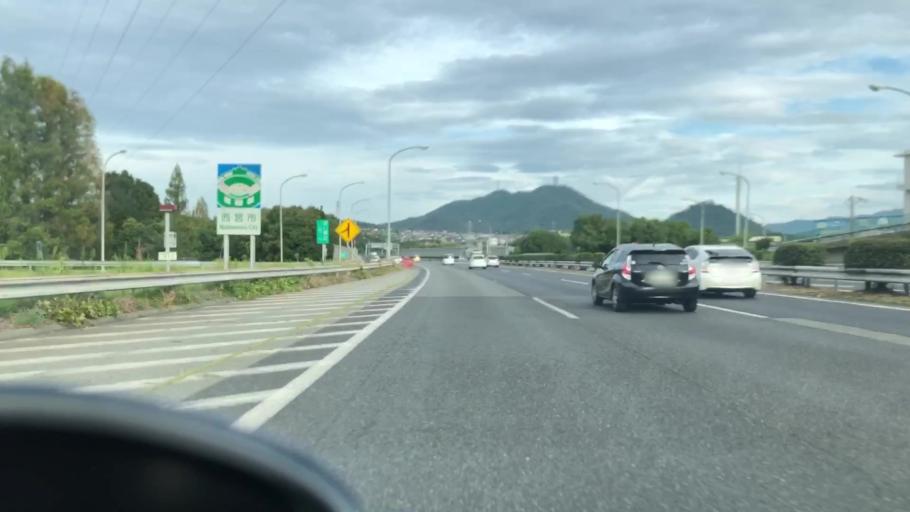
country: JP
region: Hyogo
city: Sandacho
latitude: 34.8389
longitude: 135.2338
